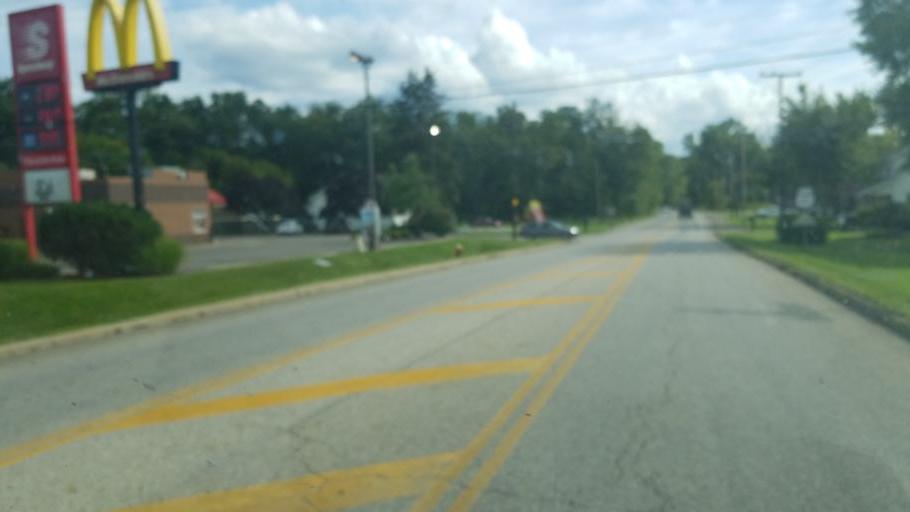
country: US
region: Ohio
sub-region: Carroll County
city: Lake Mohawk
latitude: 40.6761
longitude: -81.2611
